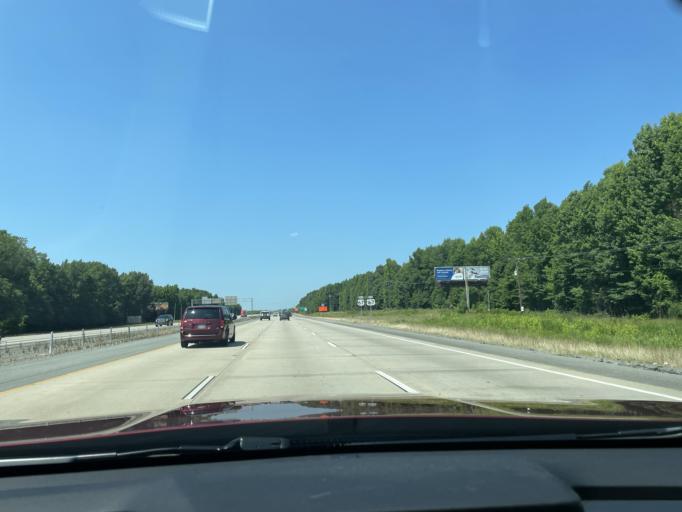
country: US
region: Arkansas
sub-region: Pulaski County
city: Jacksonville
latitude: 34.8546
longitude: -92.1375
